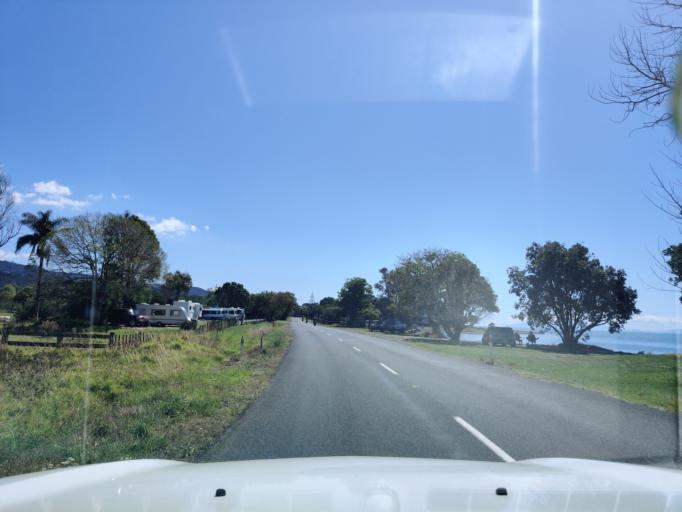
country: NZ
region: Waikato
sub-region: Thames-Coromandel District
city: Thames
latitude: -37.0505
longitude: 175.3003
